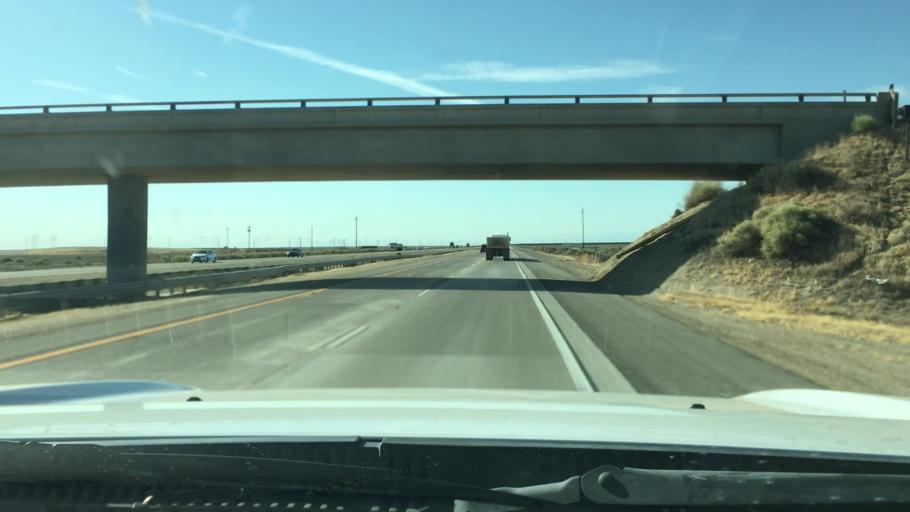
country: US
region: California
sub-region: Kern County
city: Lost Hills
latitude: 35.5589
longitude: -119.5992
